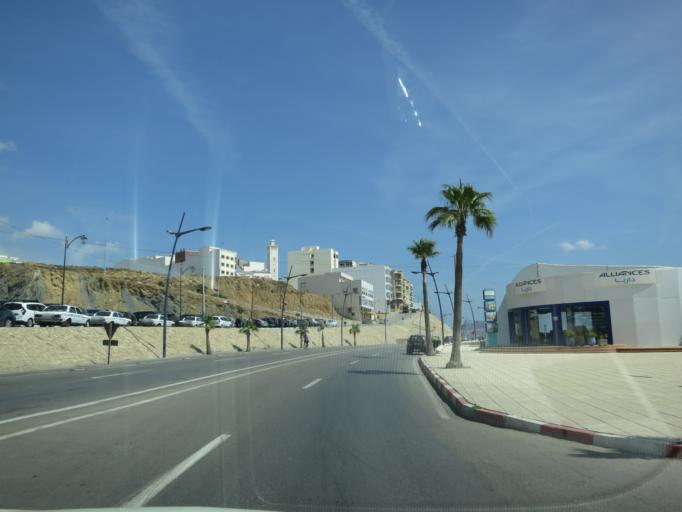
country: ES
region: Ceuta
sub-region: Ceuta
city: Ceuta
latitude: 35.8510
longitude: -5.3516
